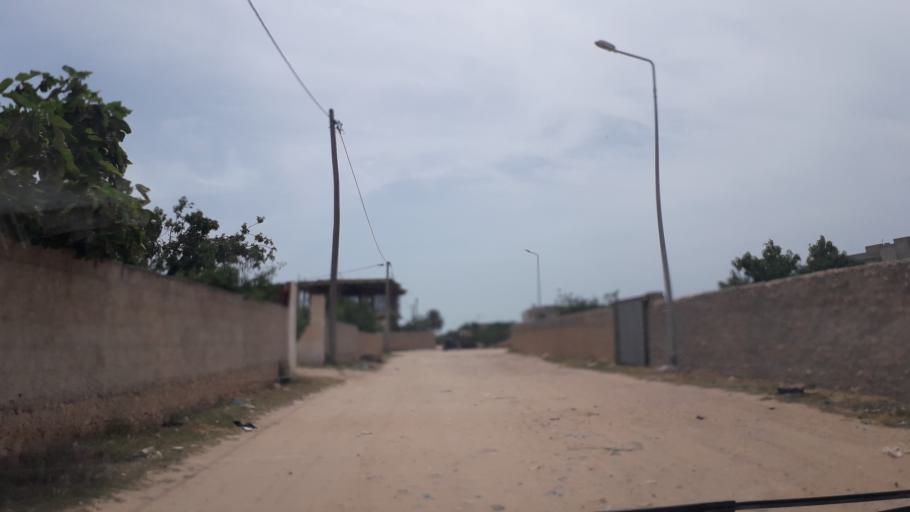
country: TN
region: Safaqis
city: Al Qarmadah
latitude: 34.8086
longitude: 10.7724
